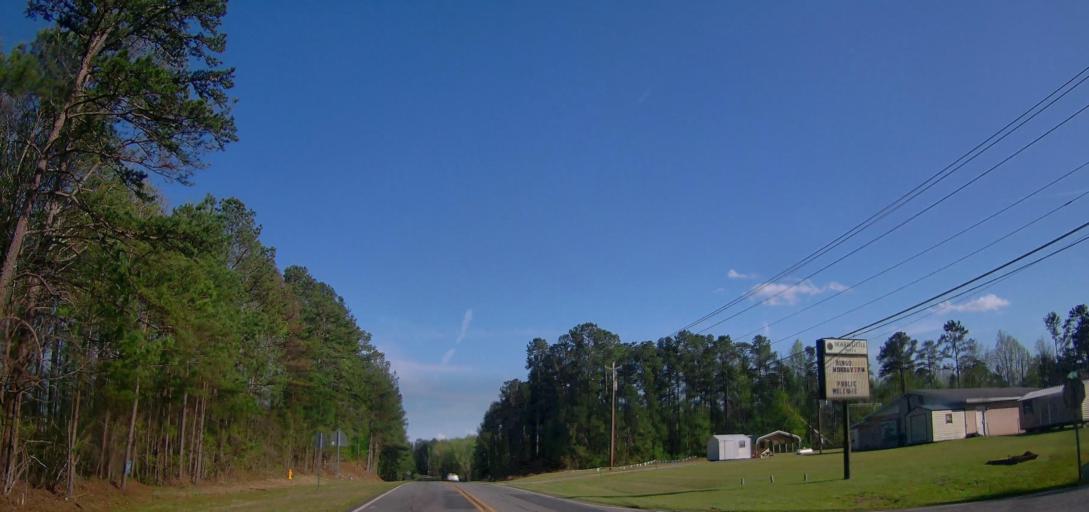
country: US
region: Georgia
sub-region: Baldwin County
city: Milledgeville
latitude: 33.1470
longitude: -83.2556
